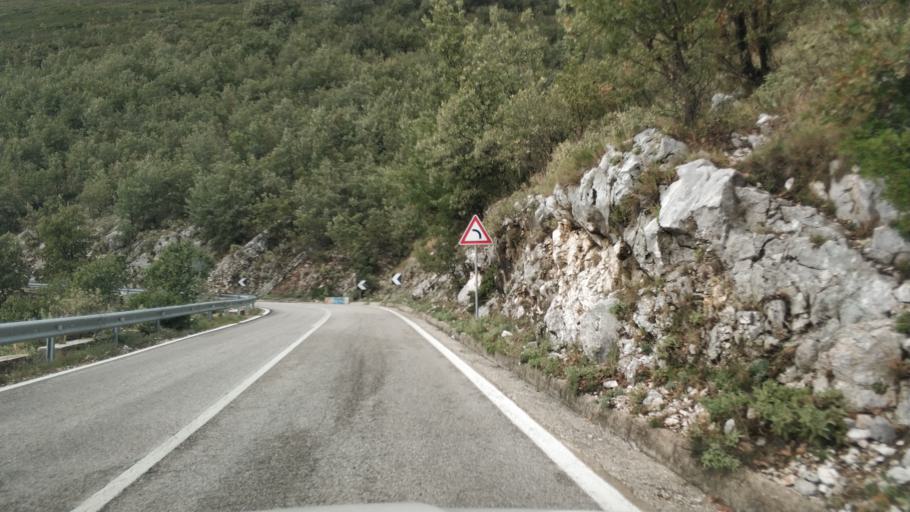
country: AL
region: Vlore
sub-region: Rrethi i Vlores
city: Vranisht
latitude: 40.1860
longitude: 19.6064
